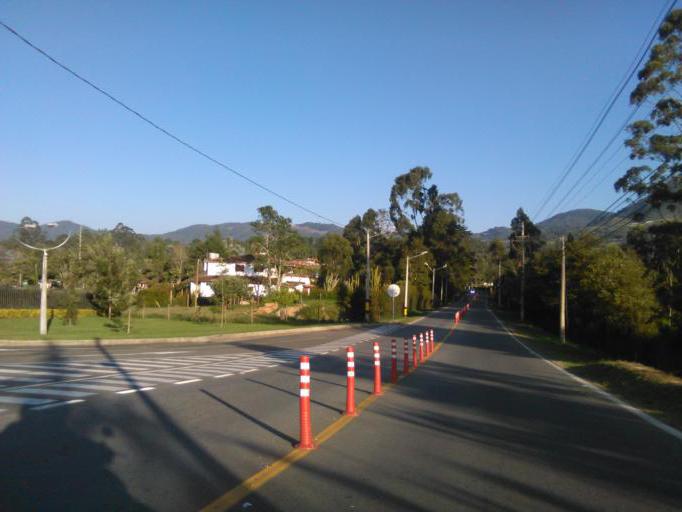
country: CO
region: Antioquia
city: La Ceja
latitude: 6.0238
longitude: -75.4128
